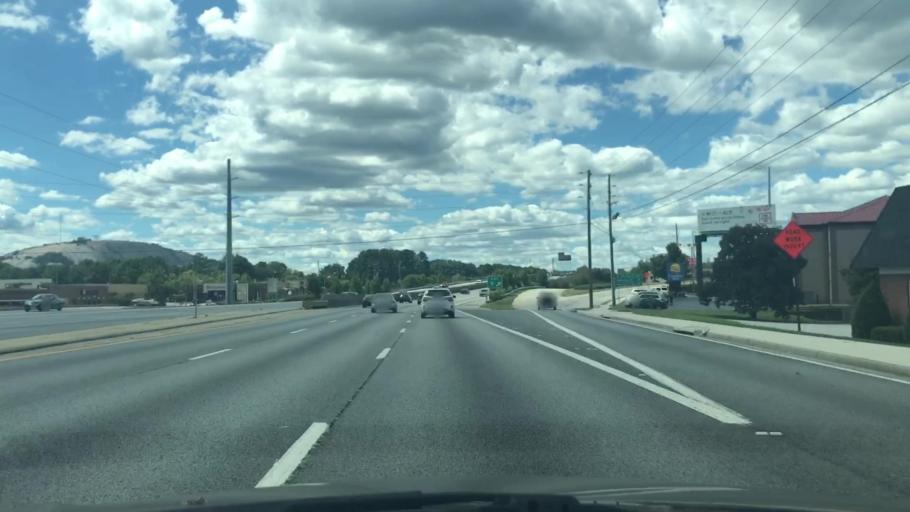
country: US
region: Georgia
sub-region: Gwinnett County
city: Mountain Park
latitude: 33.8230
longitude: -84.1148
